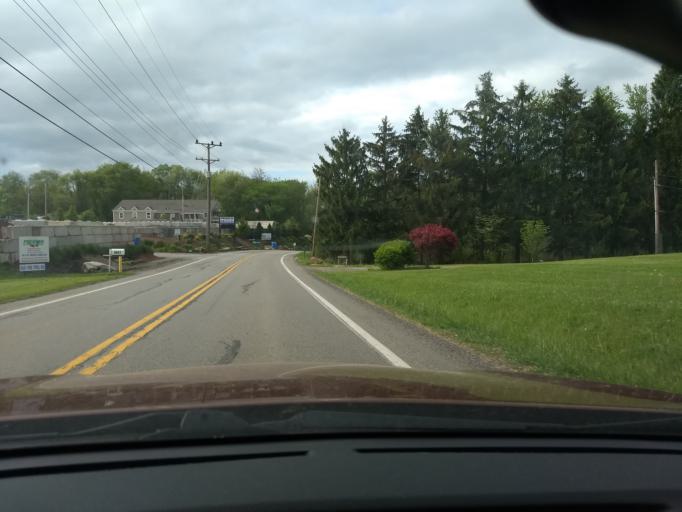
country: US
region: Pennsylvania
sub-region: Allegheny County
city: Russellton
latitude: 40.5979
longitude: -79.8892
